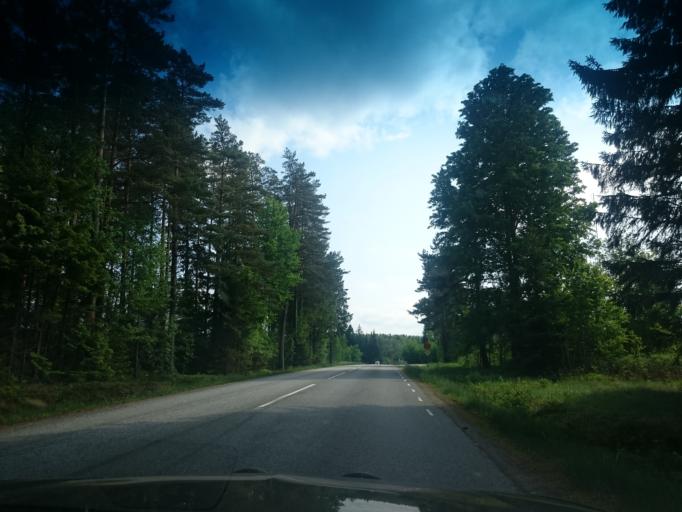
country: SE
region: Joenkoeping
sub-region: Vetlanda Kommun
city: Vetlanda
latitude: 57.4119
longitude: 15.0020
